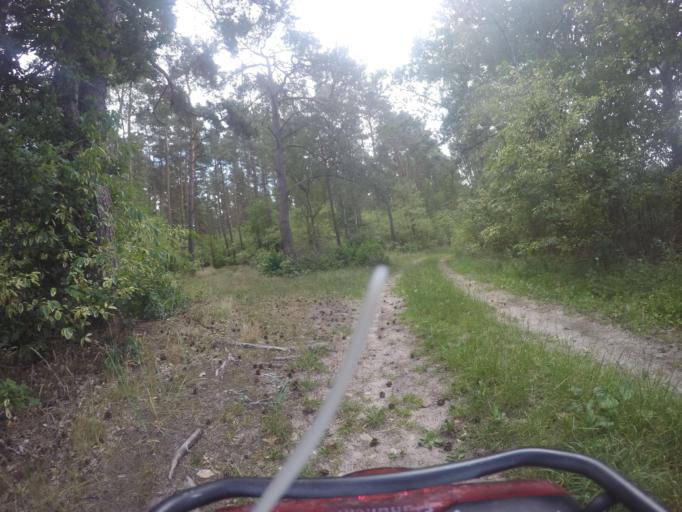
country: DE
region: Lower Saxony
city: Dahlem
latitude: 53.2217
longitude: 10.7329
